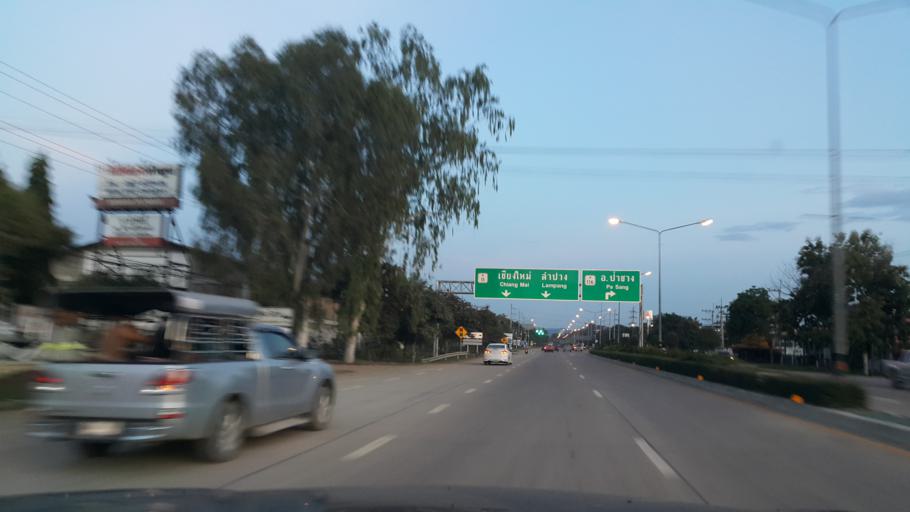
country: TH
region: Lamphun
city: Lamphun
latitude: 18.5581
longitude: 99.0394
